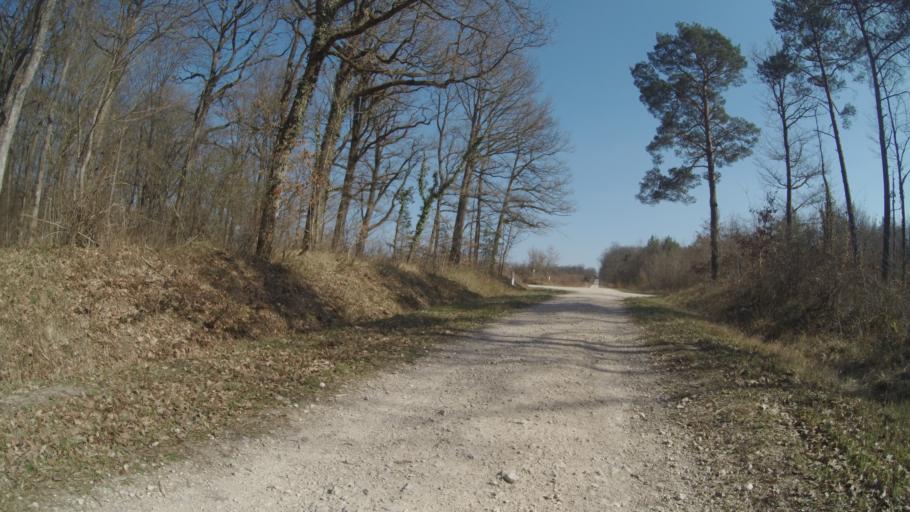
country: FR
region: Centre
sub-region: Departement du Loiret
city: Chanteau
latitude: 47.9493
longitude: 1.9620
